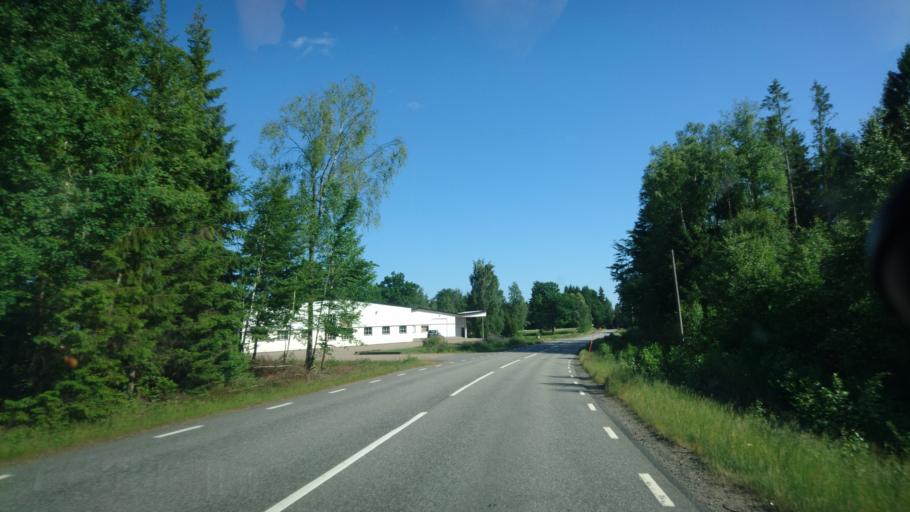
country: SE
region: Skane
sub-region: Osby Kommun
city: Lonsboda
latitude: 56.4231
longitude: 14.2827
